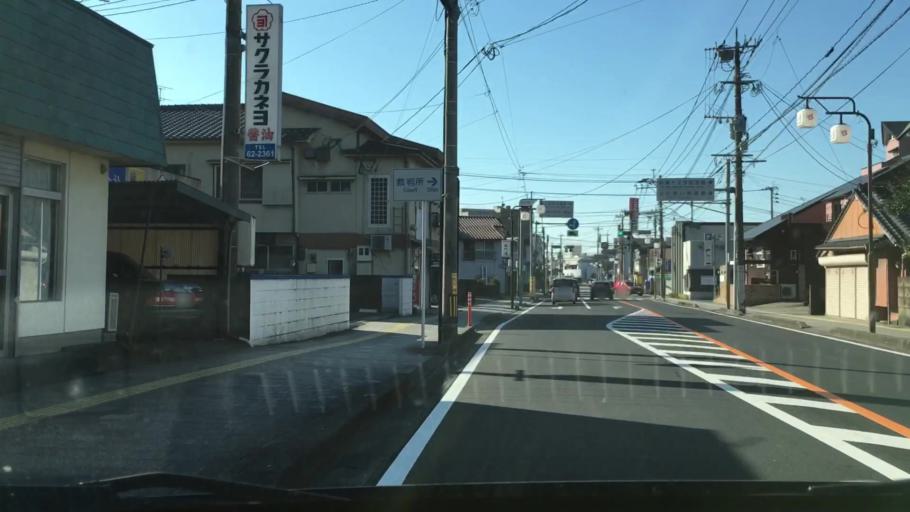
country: JP
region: Kagoshima
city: Kajiki
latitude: 31.7417
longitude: 130.6683
